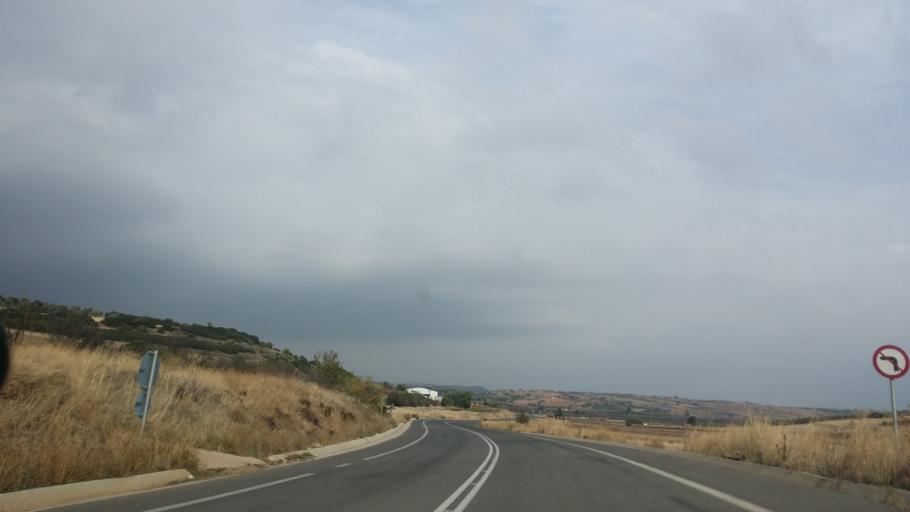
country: GR
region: Central Greece
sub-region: Nomos Voiotias
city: Thespies
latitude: 38.2796
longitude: 23.1203
